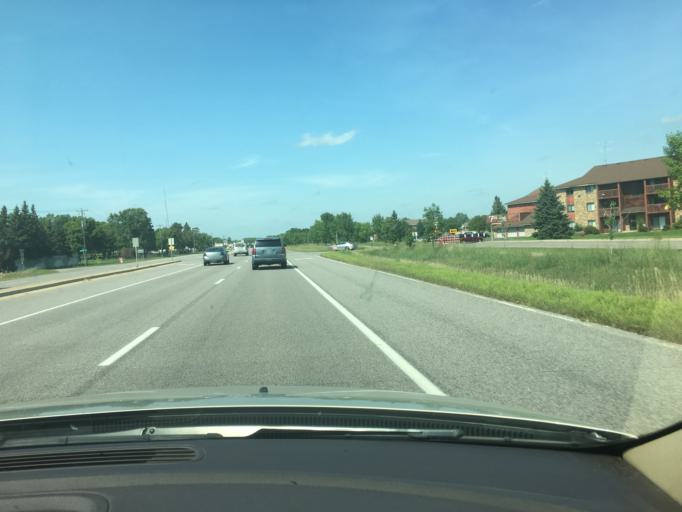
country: US
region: Minnesota
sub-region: Stearns County
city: Saint Cloud
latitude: 45.5280
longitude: -94.1630
